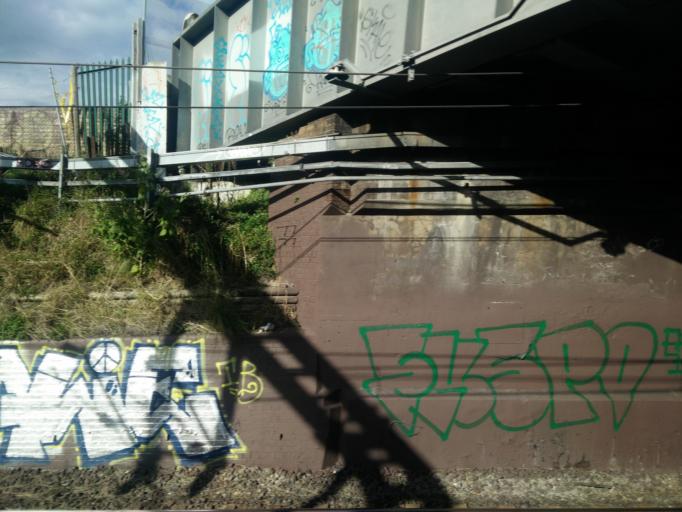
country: AU
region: New South Wales
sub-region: Marrickville
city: Newtown
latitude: -33.8979
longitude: 151.1816
